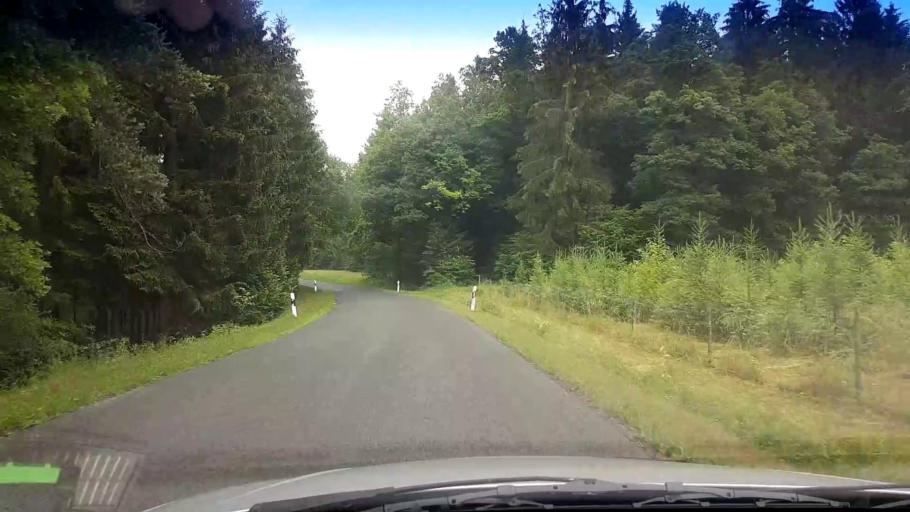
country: DE
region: Bavaria
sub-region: Upper Franconia
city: Wattendorf
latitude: 50.0590
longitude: 11.1094
